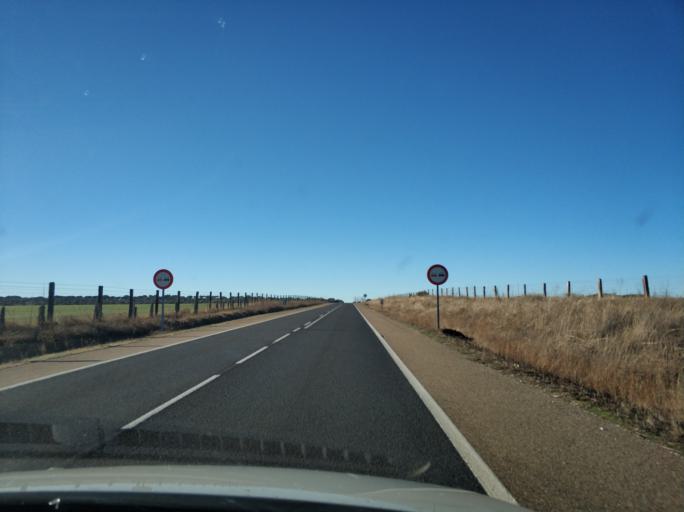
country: ES
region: Castille and Leon
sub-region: Provincia de Salamanca
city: Vecinos
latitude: 40.7978
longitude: -5.8577
